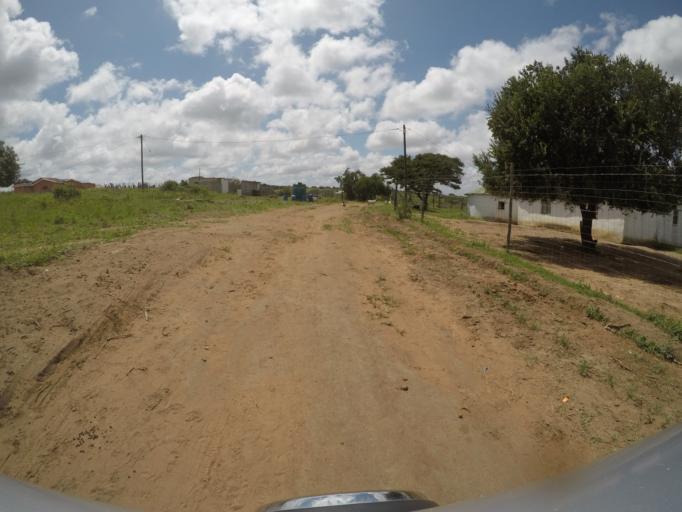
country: ZA
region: KwaZulu-Natal
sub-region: uThungulu District Municipality
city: Empangeni
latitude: -28.5869
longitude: 31.8413
